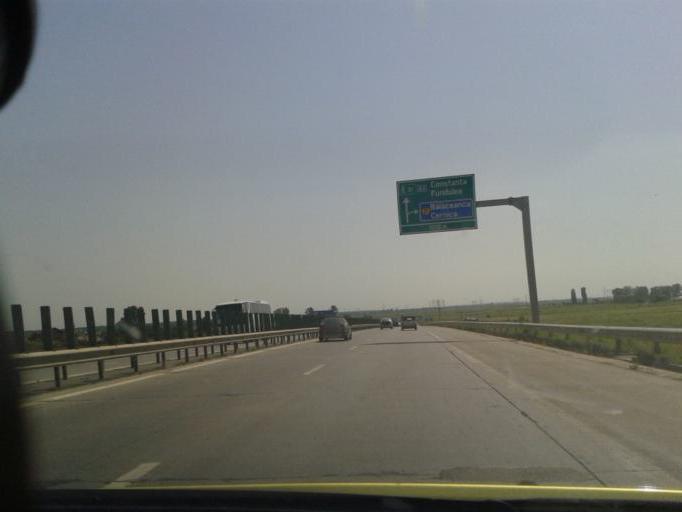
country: RO
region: Ilfov
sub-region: Comuna Cernica
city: Caldararu
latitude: 44.4086
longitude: 26.2612
